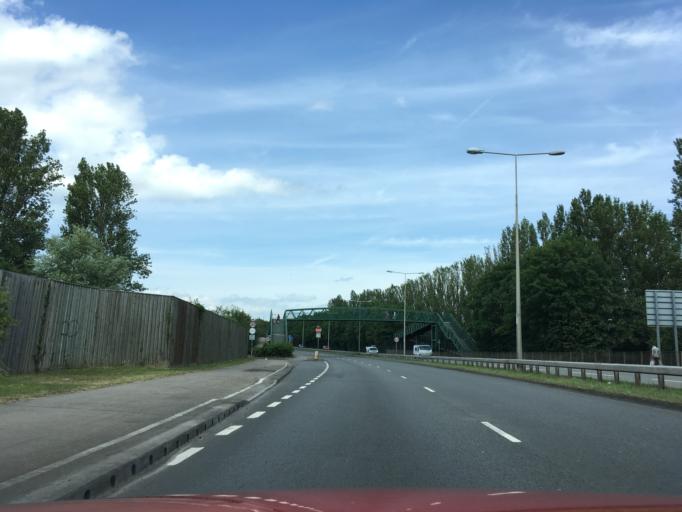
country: GB
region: Wales
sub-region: Newport
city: Nash
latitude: 51.5790
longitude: -2.9454
